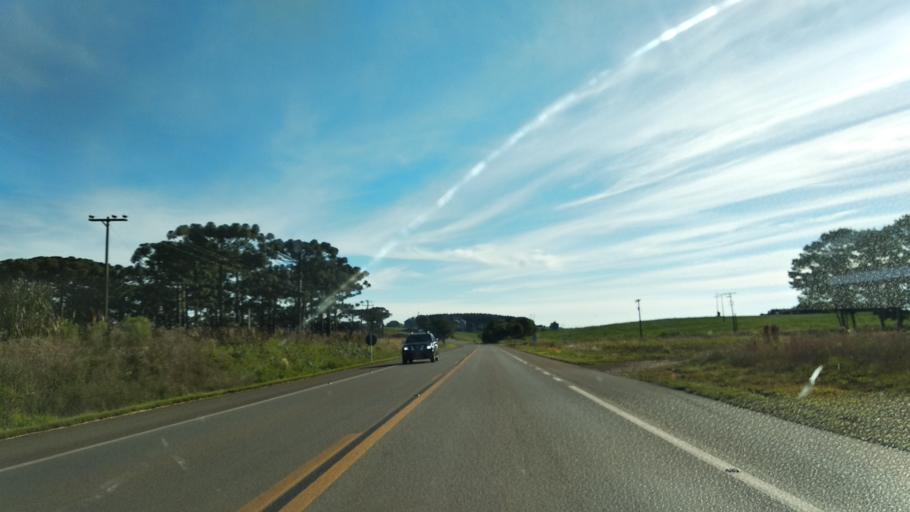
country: BR
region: Santa Catarina
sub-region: Celso Ramos
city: Celso Ramos
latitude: -27.5269
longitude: -51.3711
